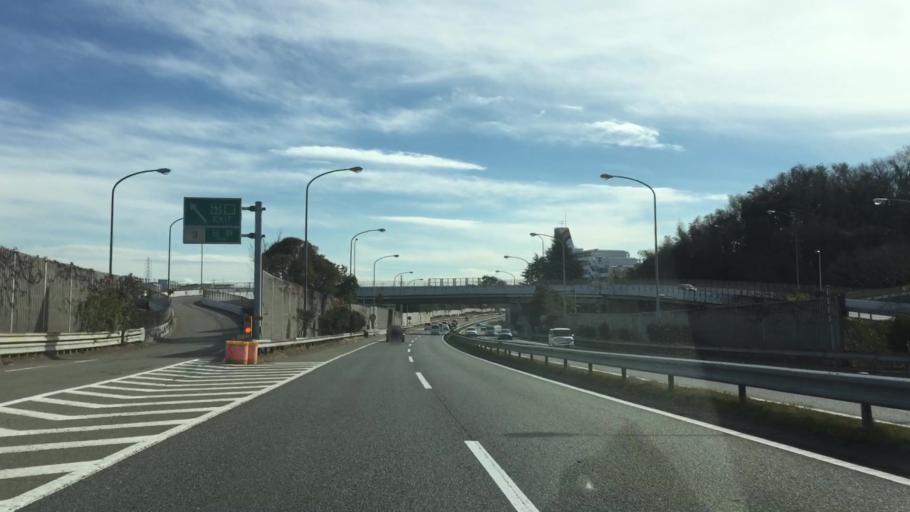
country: JP
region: Kanagawa
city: Kamakura
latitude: 35.3835
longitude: 139.5833
